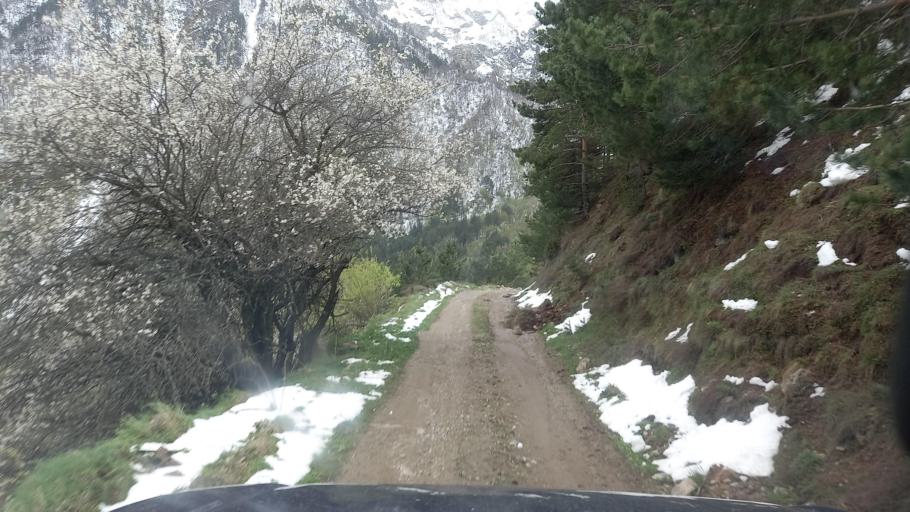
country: RU
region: North Ossetia
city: Mizur
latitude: 42.8007
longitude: 43.9333
